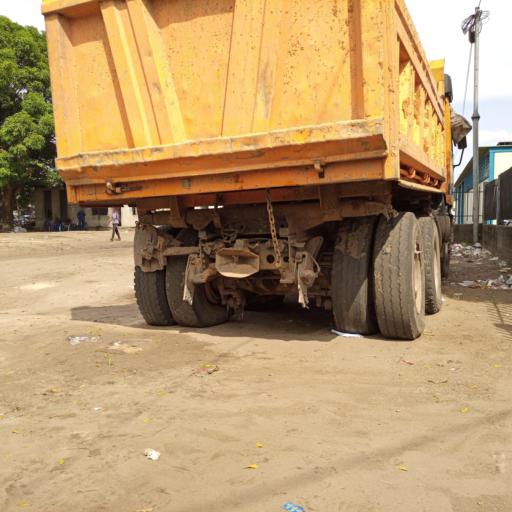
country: CD
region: Kinshasa
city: Masina
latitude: -4.3999
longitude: 15.3720
